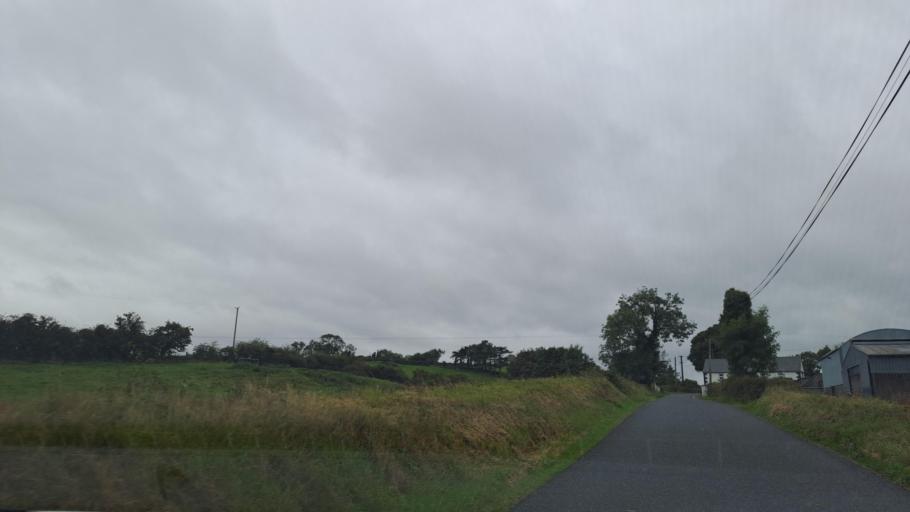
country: IE
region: Ulster
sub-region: An Cabhan
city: Kingscourt
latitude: 54.0092
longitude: -6.8751
